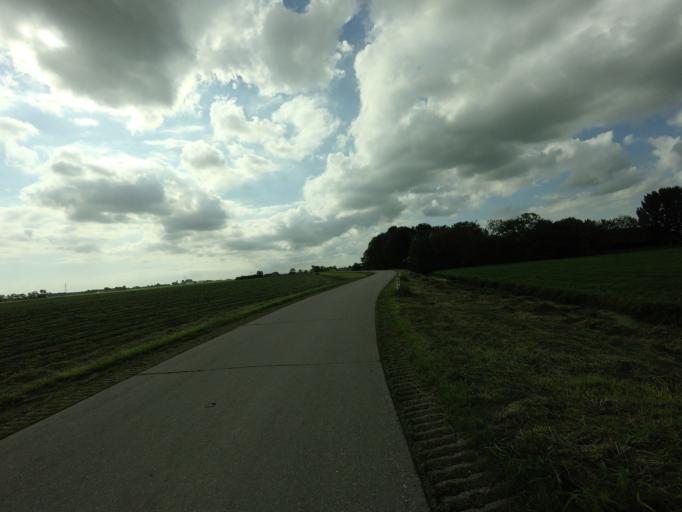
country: NL
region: Friesland
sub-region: Gemeente Littenseradiel
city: Wommels
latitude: 53.0731
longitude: 5.6056
